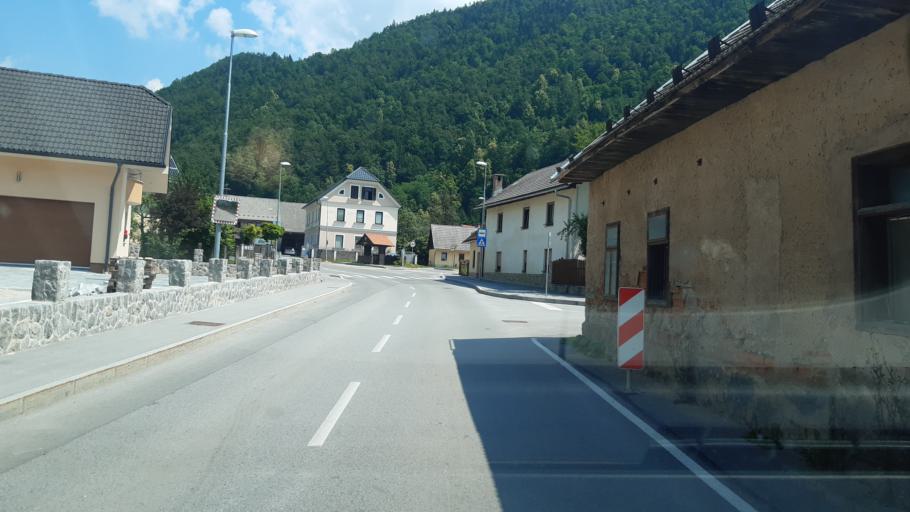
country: SI
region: Cerklje na Gorenjskem
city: Cerklje na Gorenjskem
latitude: 46.2621
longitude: 14.4930
